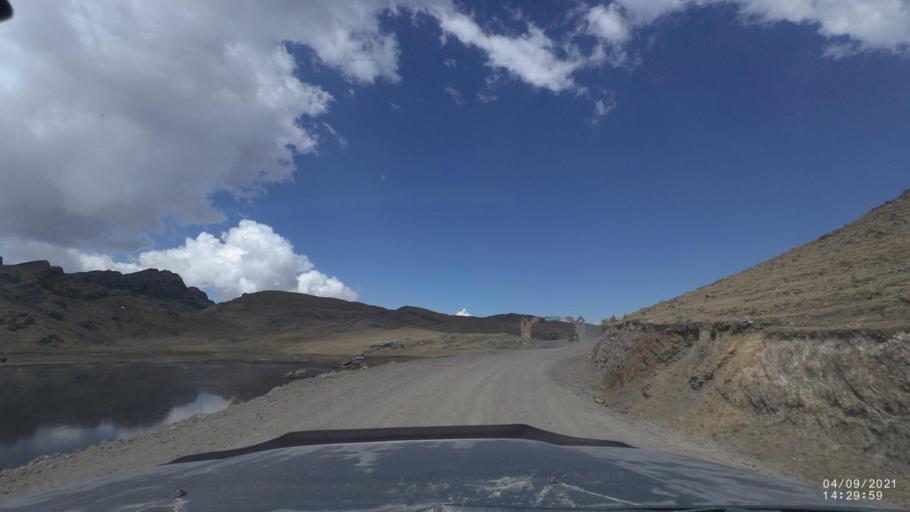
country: BO
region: Cochabamba
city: Sipe Sipe
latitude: -17.2432
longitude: -66.3985
